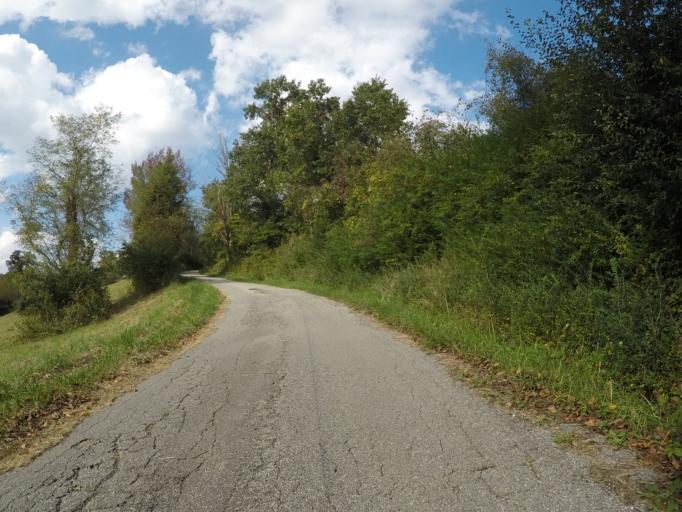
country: US
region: West Virginia
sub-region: Wayne County
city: Lavalette
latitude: 38.3580
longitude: -82.4552
